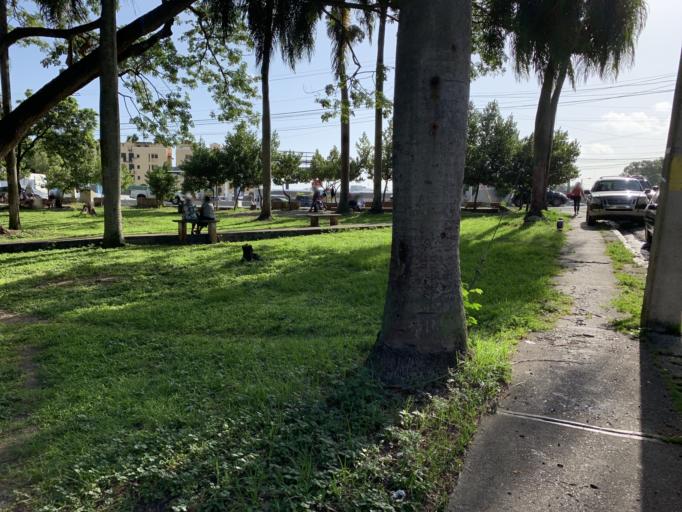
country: DO
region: Nacional
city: Santo Domingo
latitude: 18.4840
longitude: -69.9680
